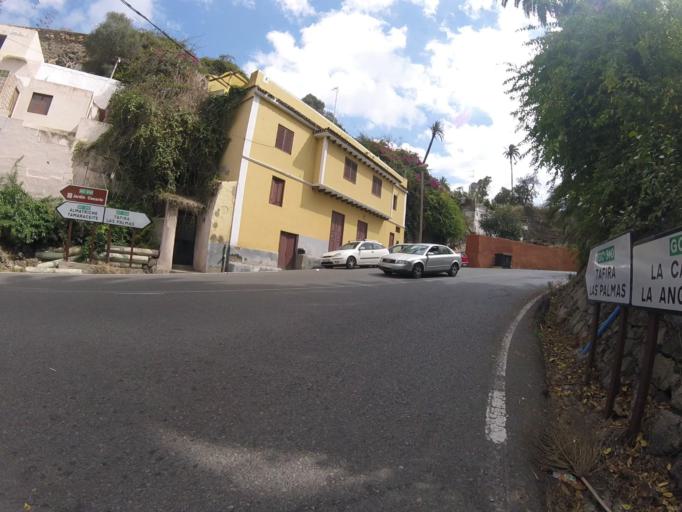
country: ES
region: Canary Islands
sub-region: Provincia de Las Palmas
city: Santa Brigida
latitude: 28.0587
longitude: -15.4661
